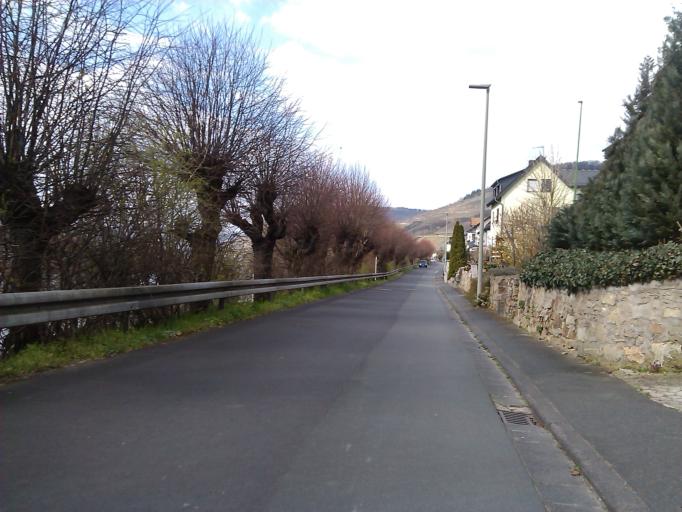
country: DE
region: Rheinland-Pfalz
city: Niederheimbach
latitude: 50.0326
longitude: 7.8219
